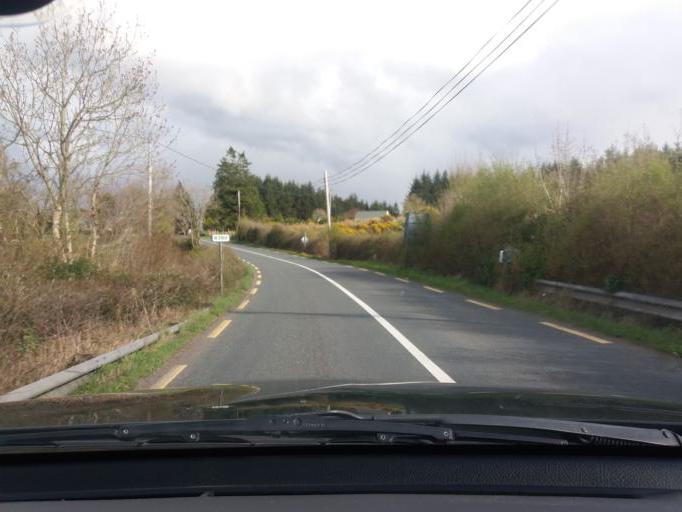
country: IE
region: Connaught
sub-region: County Leitrim
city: Manorhamilton
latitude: 54.3196
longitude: -8.2009
